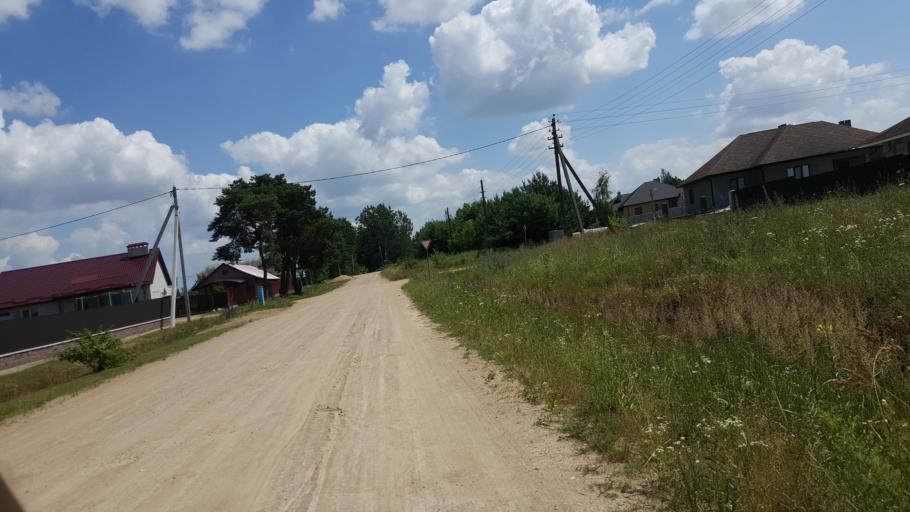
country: BY
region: Brest
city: Kamyanyets
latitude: 52.4007
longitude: 23.8447
